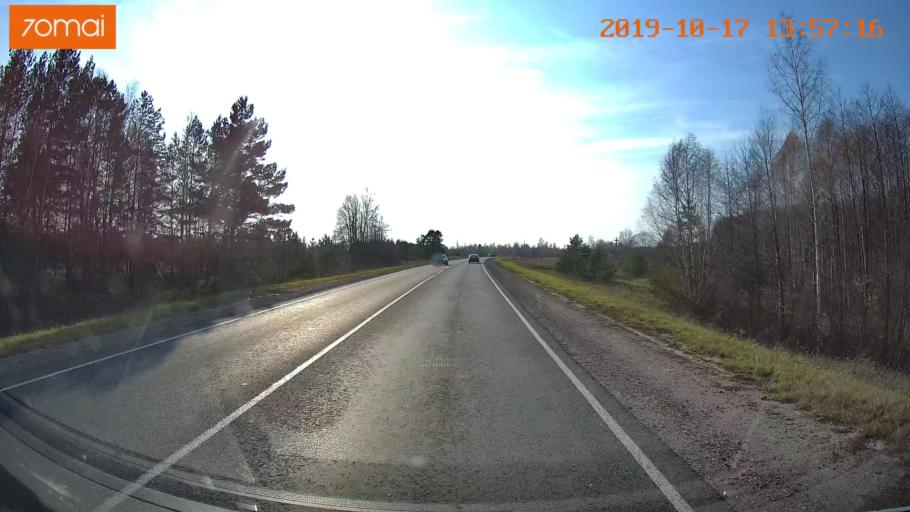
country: RU
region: Rjazan
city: Spas-Klepiki
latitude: 55.1450
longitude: 40.2500
